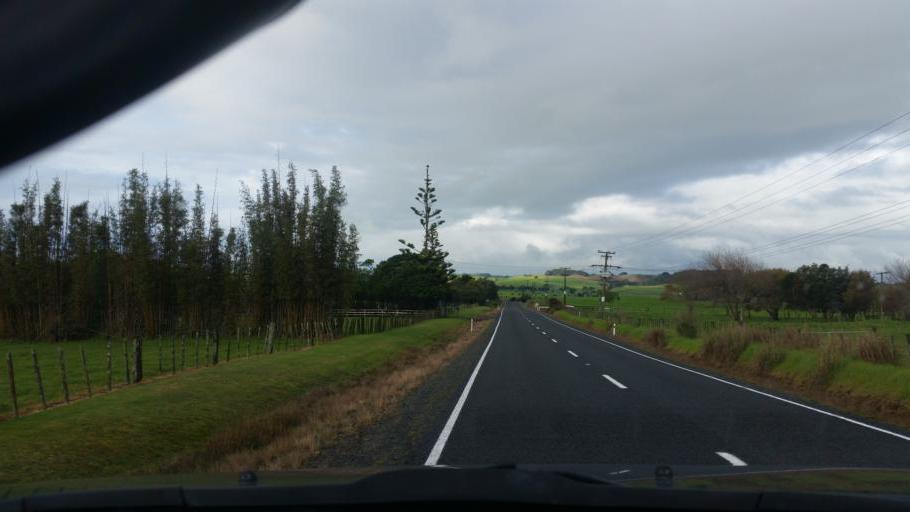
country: NZ
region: Northland
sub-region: Kaipara District
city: Dargaville
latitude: -35.9480
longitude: 173.7932
